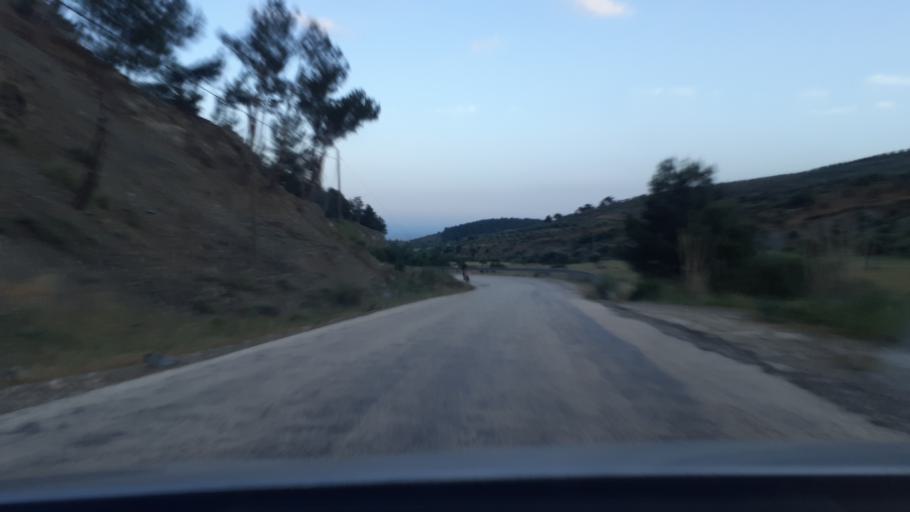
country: TR
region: Hatay
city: Kirikhan
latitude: 36.5147
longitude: 36.3193
